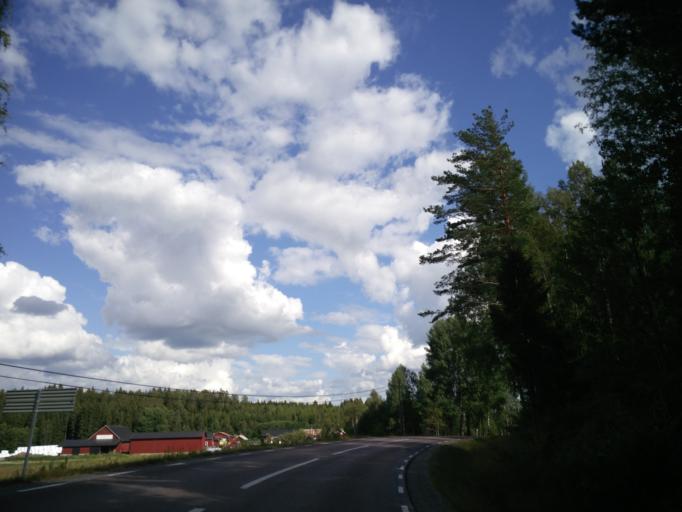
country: SE
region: Vaermland
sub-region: Sunne Kommun
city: Sunne
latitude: 59.6695
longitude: 12.9897
